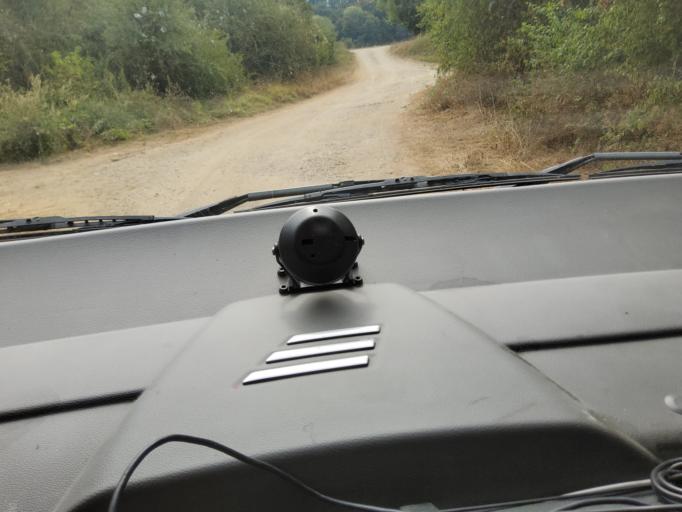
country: FR
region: Franche-Comte
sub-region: Departement du Jura
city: Choisey
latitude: 47.0137
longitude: 5.4837
